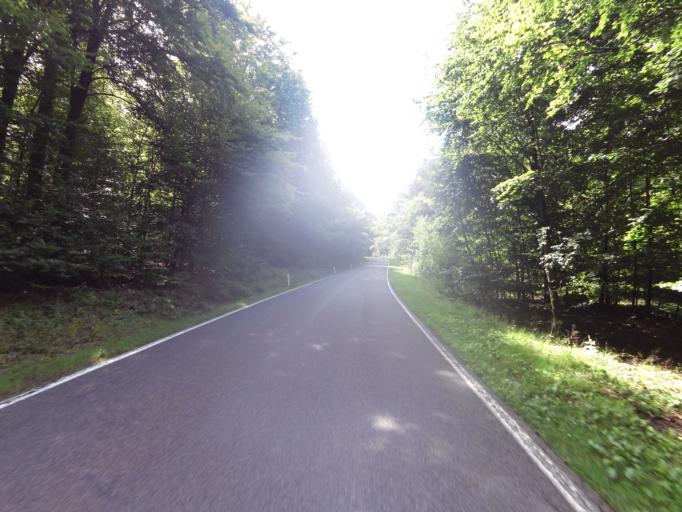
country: BE
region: Wallonia
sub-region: Province du Luxembourg
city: Saint-Hubert
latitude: 50.0687
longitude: 5.3472
